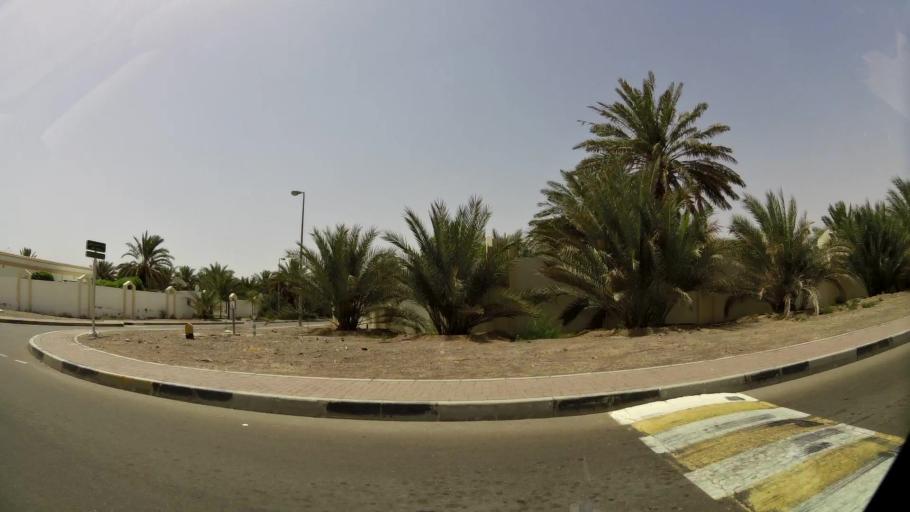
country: AE
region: Abu Dhabi
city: Al Ain
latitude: 24.1816
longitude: 55.7093
